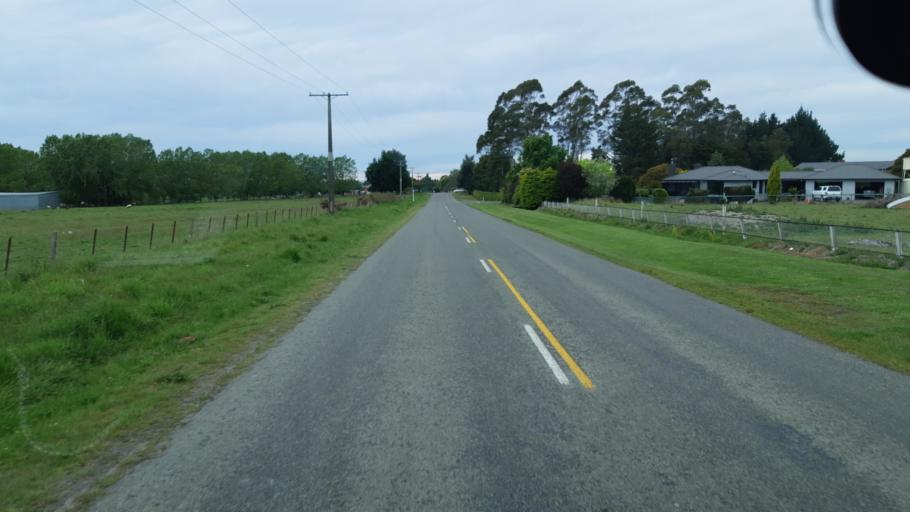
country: NZ
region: Canterbury
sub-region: Timaru District
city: Timaru
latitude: -44.4134
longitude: 171.1968
